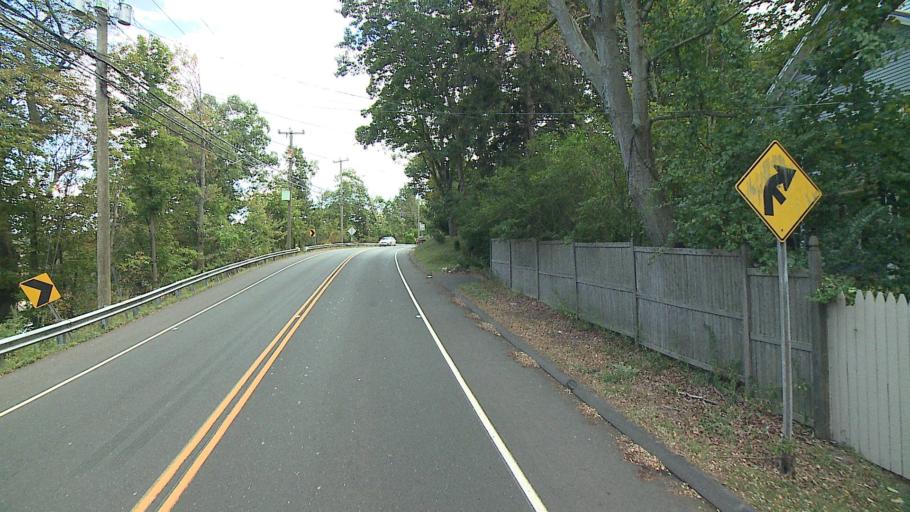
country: US
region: Connecticut
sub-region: Fairfield County
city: Westport
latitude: 41.1453
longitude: -73.3658
